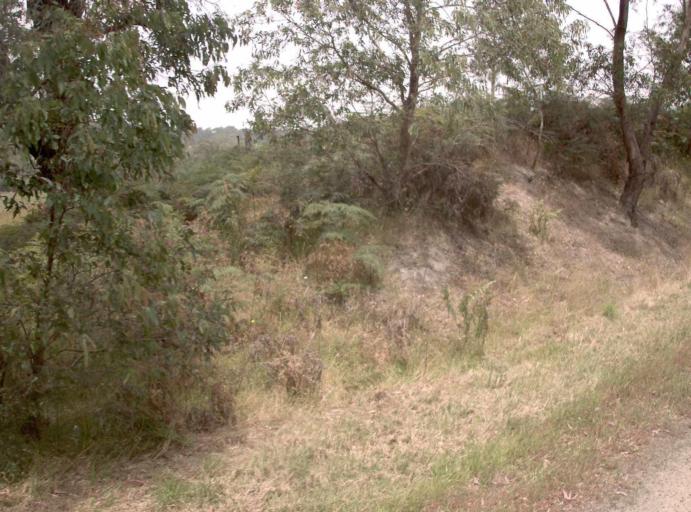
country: AU
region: Victoria
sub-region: Latrobe
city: Traralgon
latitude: -38.4603
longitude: 146.7265
